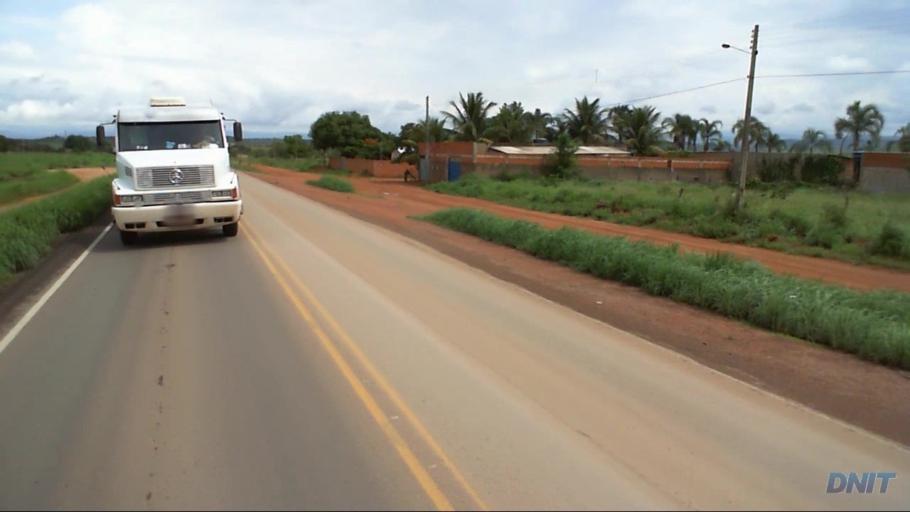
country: BR
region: Goias
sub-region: Padre Bernardo
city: Padre Bernardo
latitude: -15.2509
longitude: -48.2683
